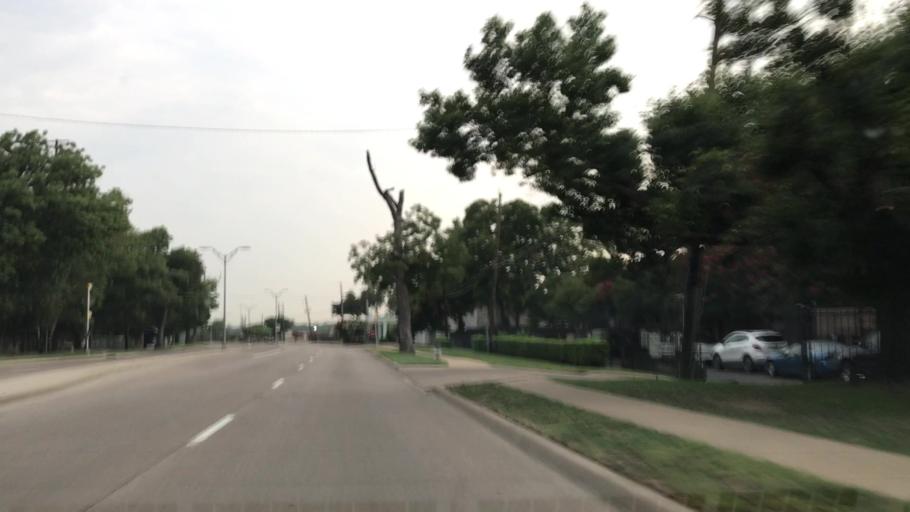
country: US
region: Texas
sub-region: Dallas County
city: Highland Park
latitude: 32.7937
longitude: -96.7161
